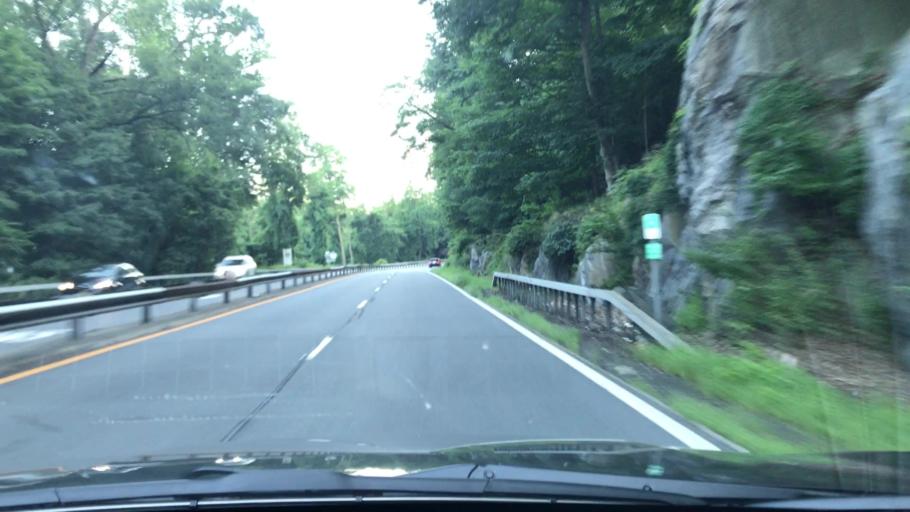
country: US
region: New York
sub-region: Westchester County
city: Greenburgh
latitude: 41.0399
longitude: -73.8382
